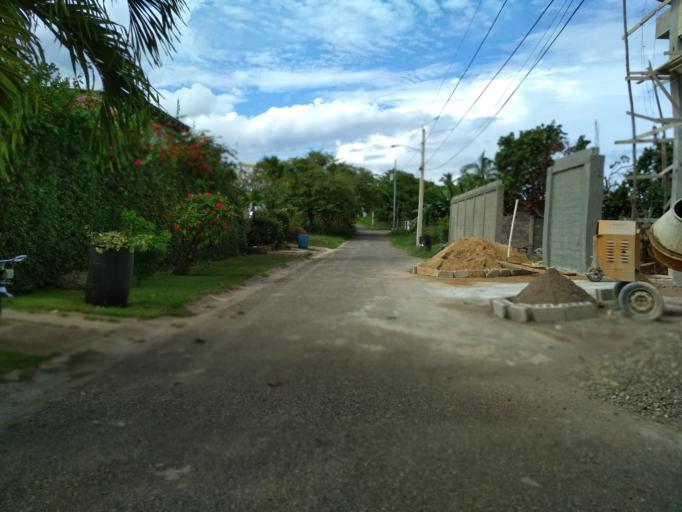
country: DO
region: Puerto Plata
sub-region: Puerto Plata
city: Puerto Plata
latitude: 19.8080
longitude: -70.7083
